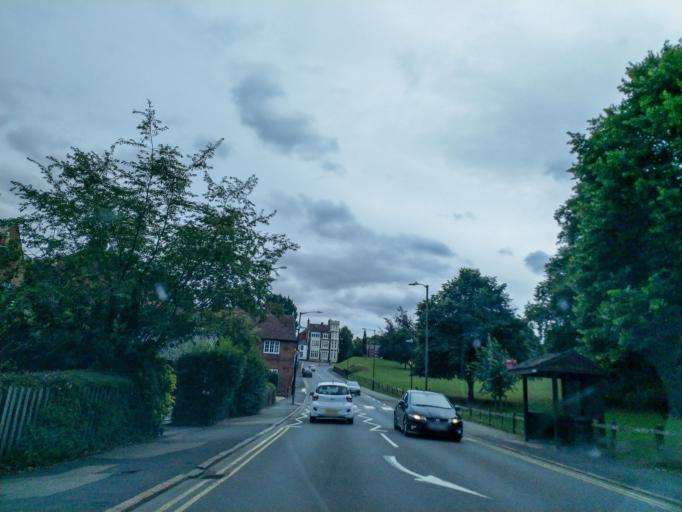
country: GB
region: England
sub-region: Warwickshire
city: Kenilworth
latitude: 52.3484
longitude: -1.5793
